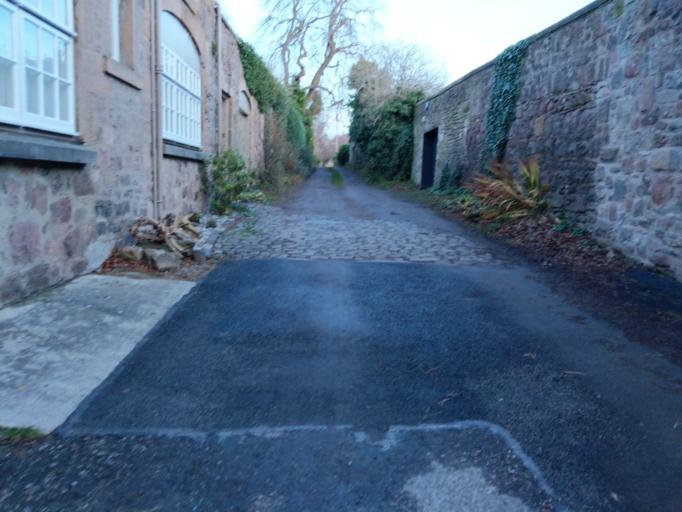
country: GB
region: Scotland
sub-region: Edinburgh
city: Edinburgh
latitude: 55.9305
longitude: -3.2150
